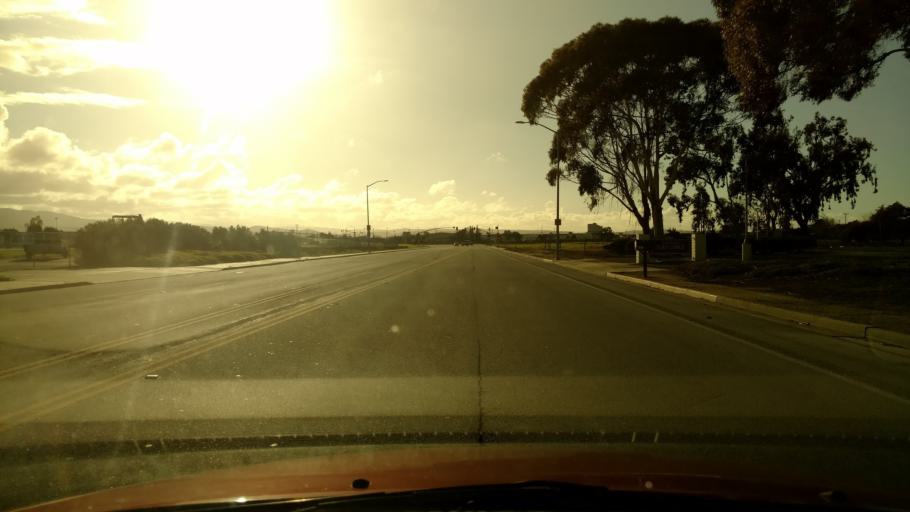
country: US
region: California
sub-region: Monterey County
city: Salinas
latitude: 36.6648
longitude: -121.6179
